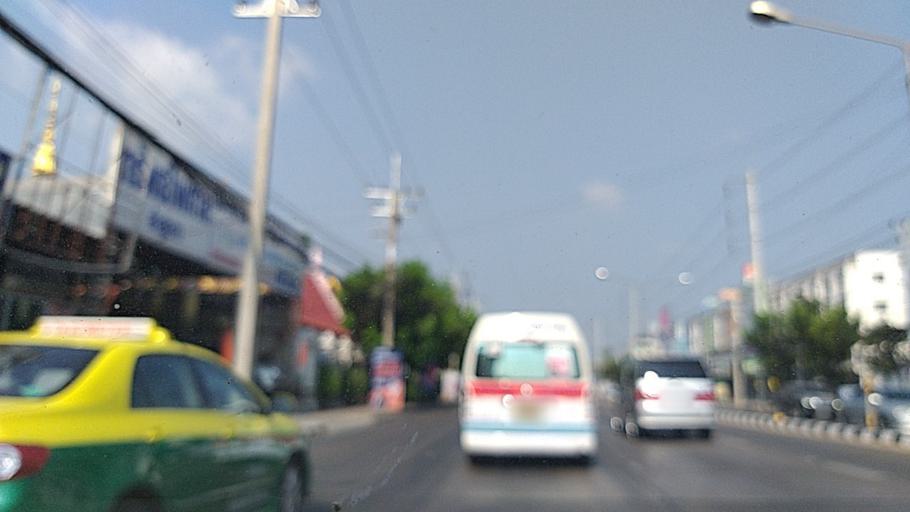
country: TH
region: Bangkok
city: Sai Mai
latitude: 13.9320
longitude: 100.6595
